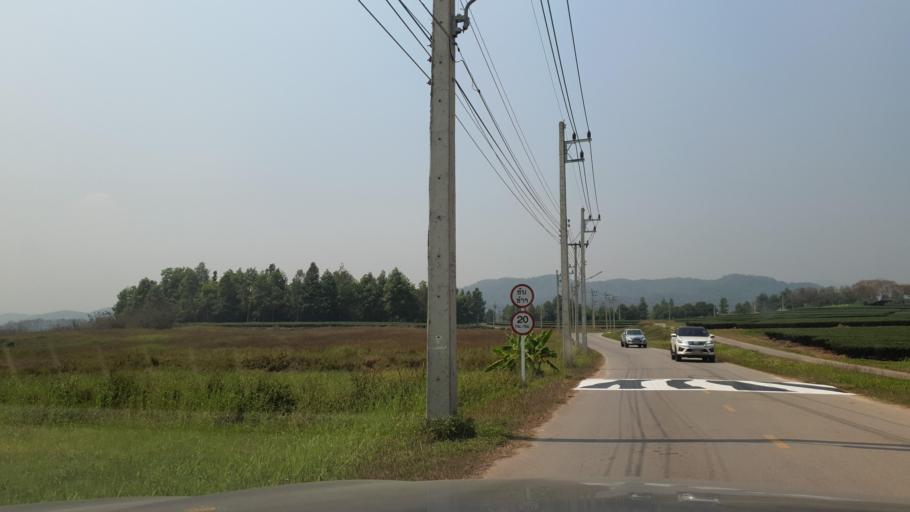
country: TH
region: Chiang Rai
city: Mae Lao
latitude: 19.8598
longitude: 99.7332
